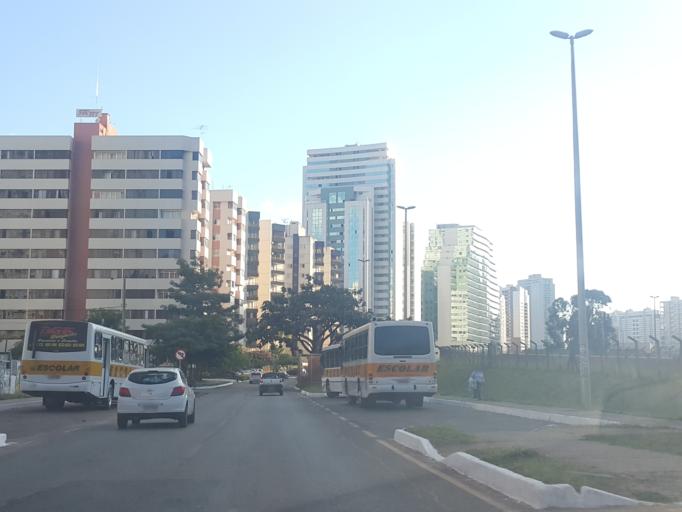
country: BR
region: Federal District
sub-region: Brasilia
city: Brasilia
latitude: -15.8397
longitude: -48.0231
